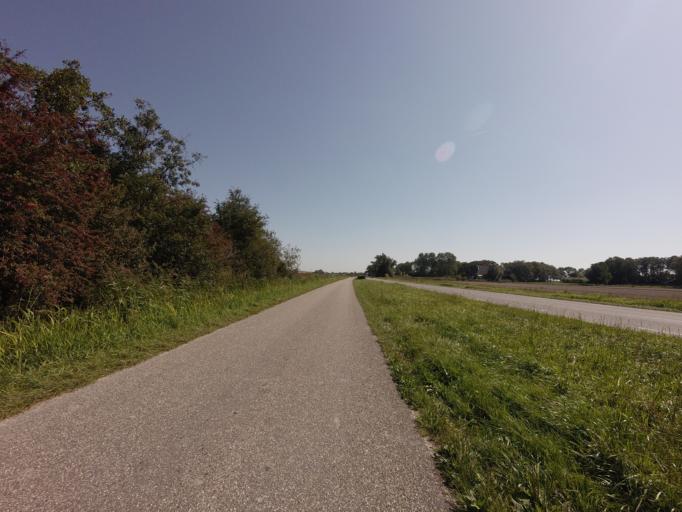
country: NL
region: Friesland
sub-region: Gemeente Dongeradeel
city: Ternaard
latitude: 53.3819
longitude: 6.0324
